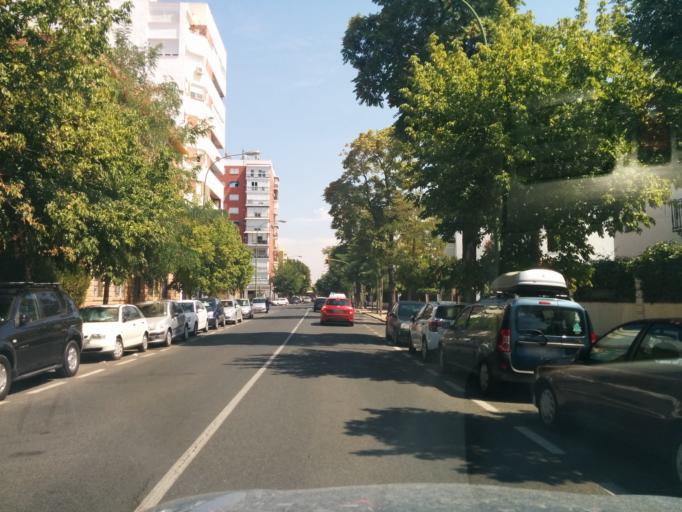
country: ES
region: Andalusia
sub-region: Provincia de Sevilla
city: Sevilla
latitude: 37.3554
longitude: -5.9873
